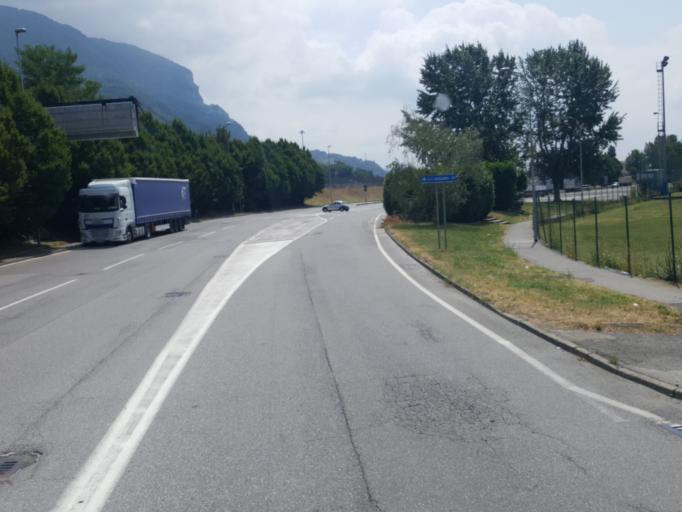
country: IT
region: Lombardy
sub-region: Provincia di Lecco
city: Pescate
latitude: 45.8383
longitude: 9.4069
